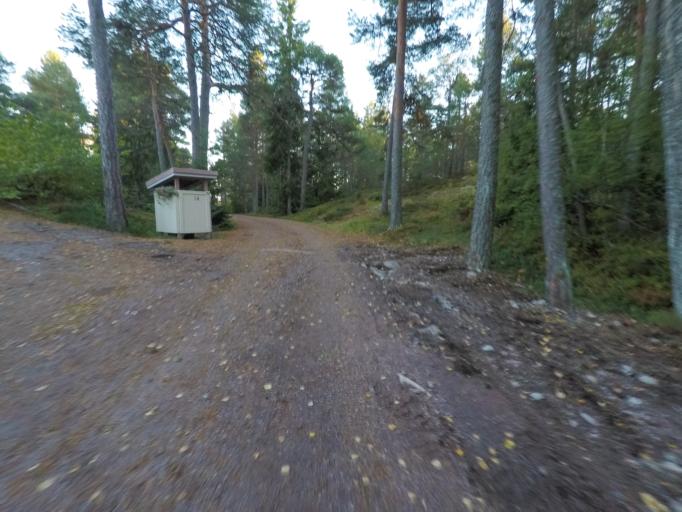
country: FI
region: Uusimaa
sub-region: Helsinki
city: Vantaa
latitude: 60.1596
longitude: 25.0746
